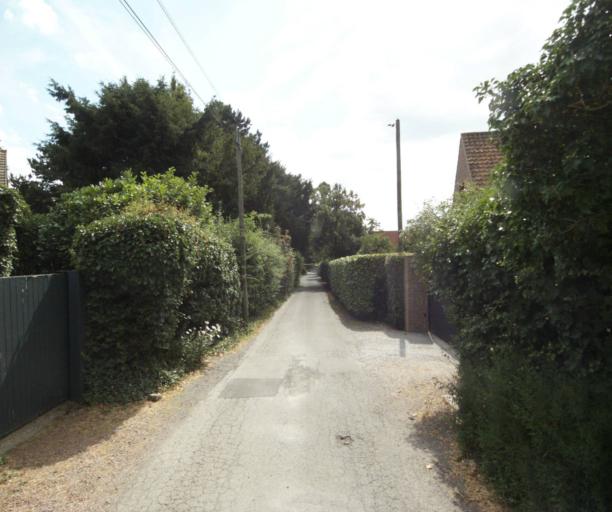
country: FR
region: Nord-Pas-de-Calais
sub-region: Departement du Nord
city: Wasquehal
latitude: 50.6845
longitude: 3.1227
